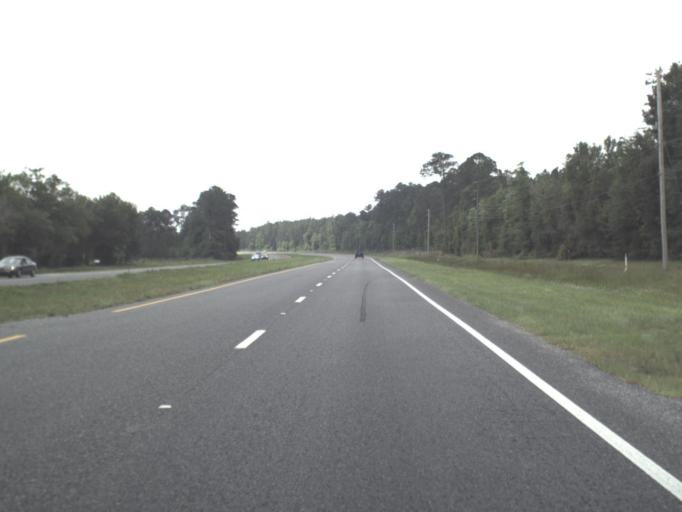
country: US
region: Florida
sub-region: Putnam County
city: Palatka
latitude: 29.8156
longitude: -81.6603
